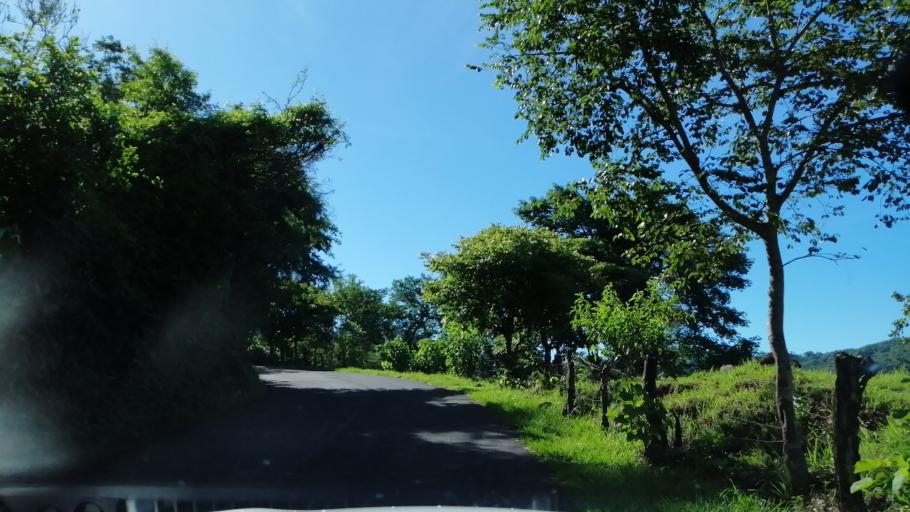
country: SV
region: Morazan
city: Corinto
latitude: 13.7904
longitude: -88.0188
